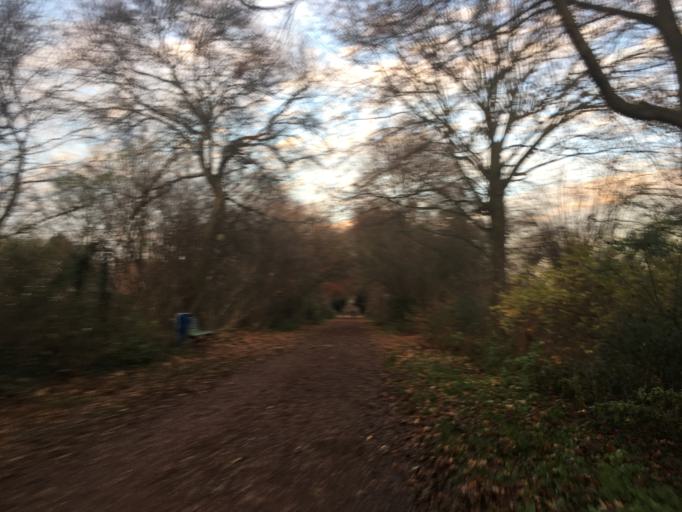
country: DE
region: Berlin
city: Stadtrandsiedlung Malchow
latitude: 52.5753
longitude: 13.4640
